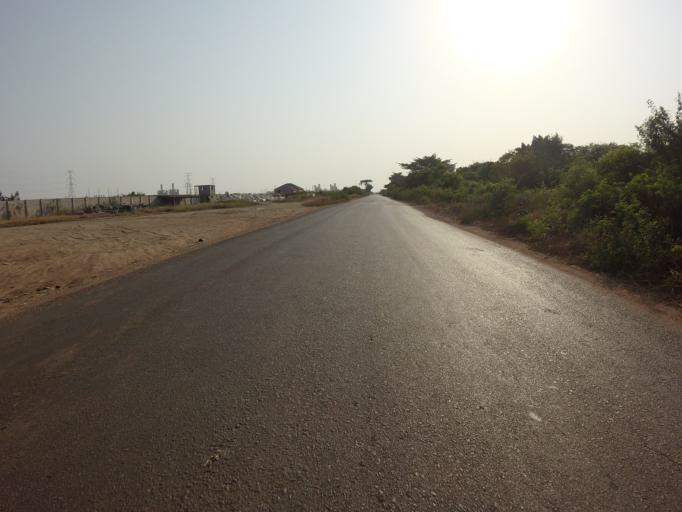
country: GH
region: Greater Accra
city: Tema
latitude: 5.6911
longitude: 0.0482
